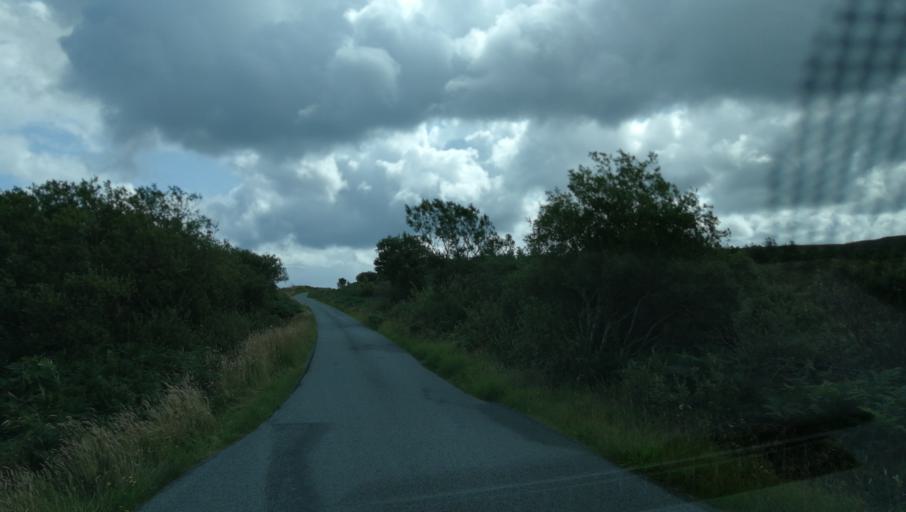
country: GB
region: Scotland
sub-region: Highland
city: Portree
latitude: 57.3812
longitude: -6.1726
